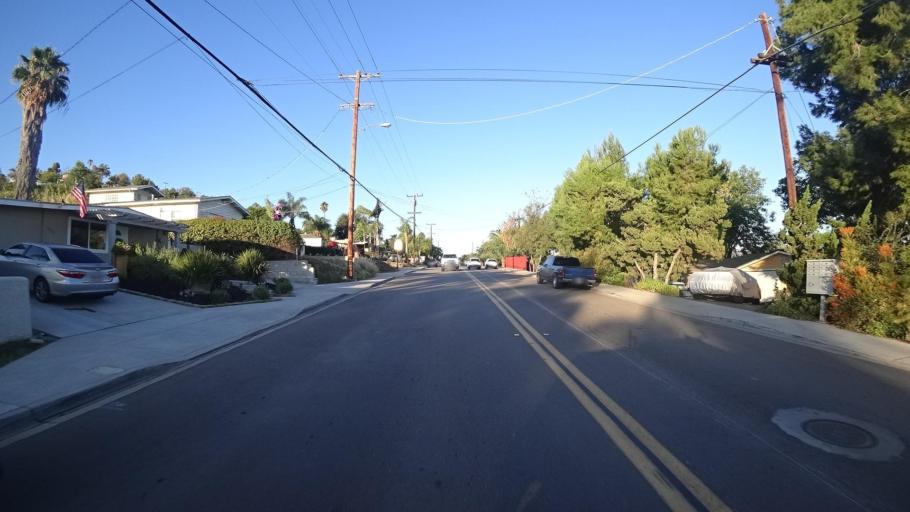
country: US
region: California
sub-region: San Diego County
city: Lakeside
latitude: 32.8562
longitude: -116.9128
